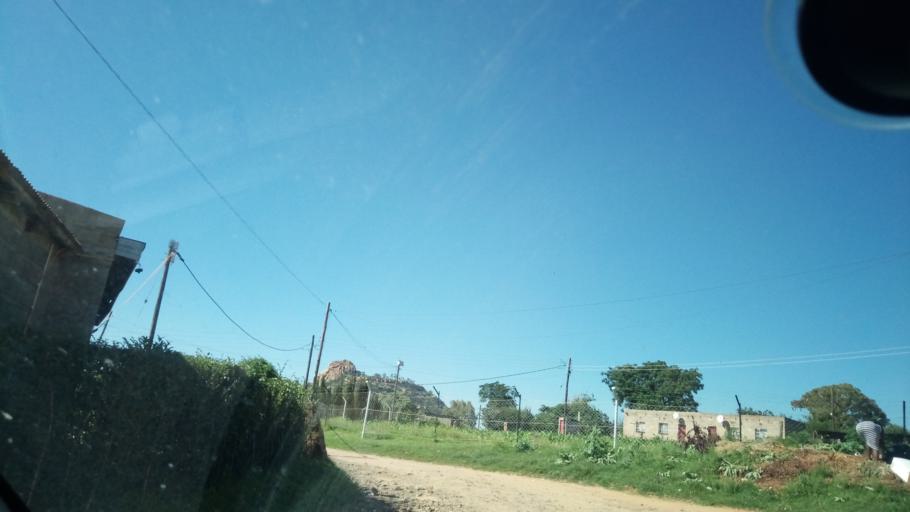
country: LS
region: Maseru
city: Maseru
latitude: -29.3522
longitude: 27.5363
